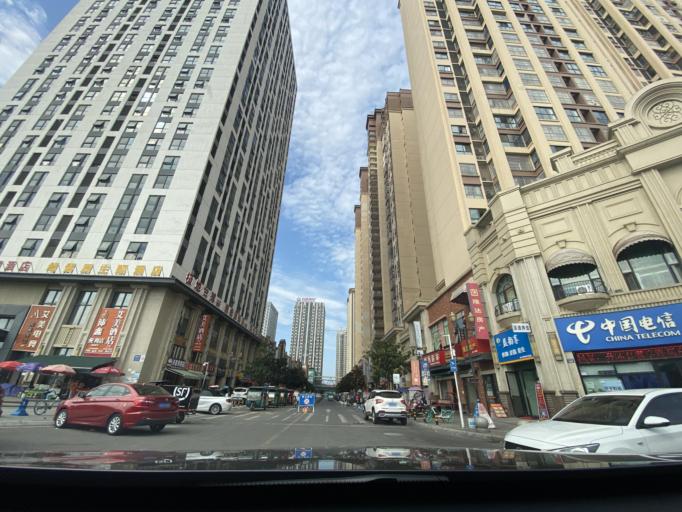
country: CN
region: Sichuan
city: Mianyang
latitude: 31.4127
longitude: 104.7820
